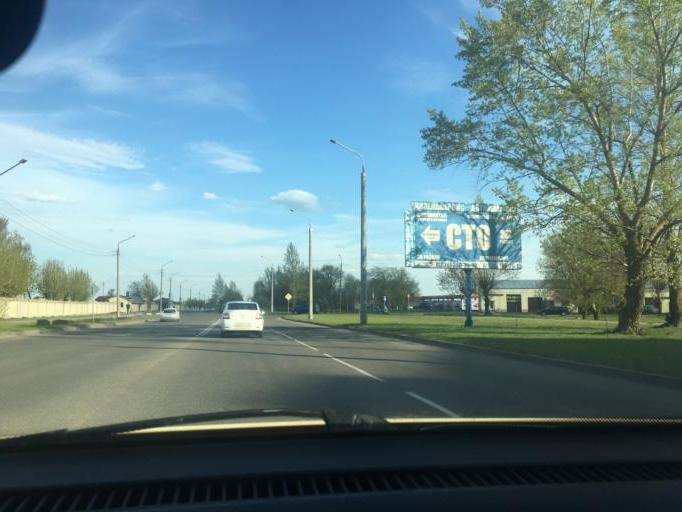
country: BY
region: Mogilev
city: Babruysk
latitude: 53.1583
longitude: 29.1723
